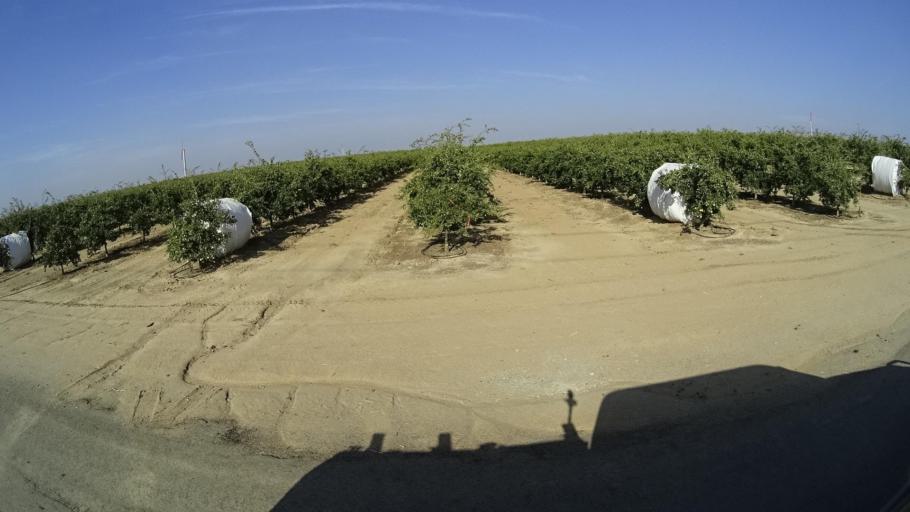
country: US
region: California
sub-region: Kern County
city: McFarland
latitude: 35.6166
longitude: -119.1714
